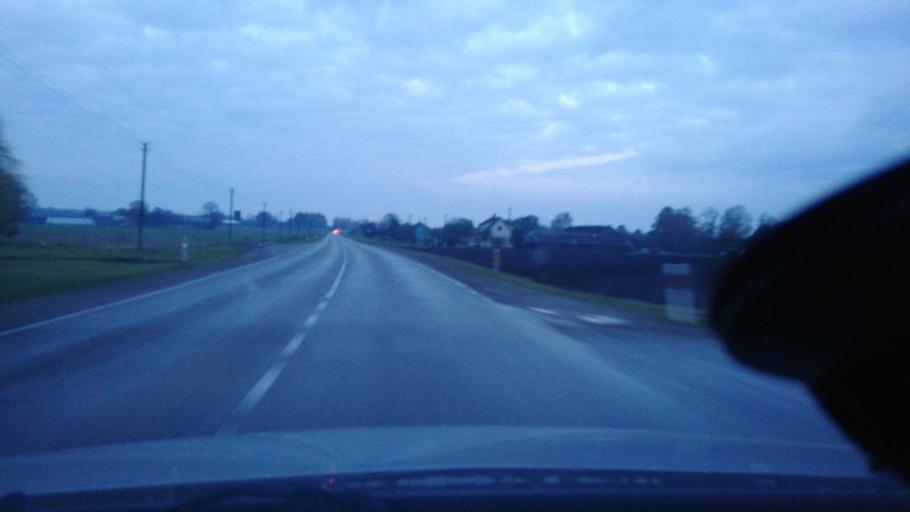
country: LT
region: Telsiu apskritis
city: Plunge
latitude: 55.8826
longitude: 21.7690
